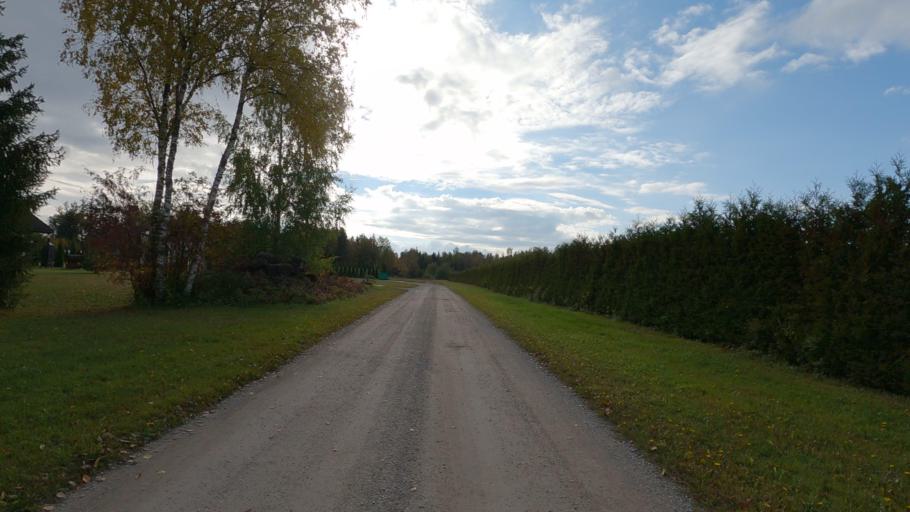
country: EE
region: Raplamaa
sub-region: Rapla vald
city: Rapla
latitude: 58.9747
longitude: 24.7778
